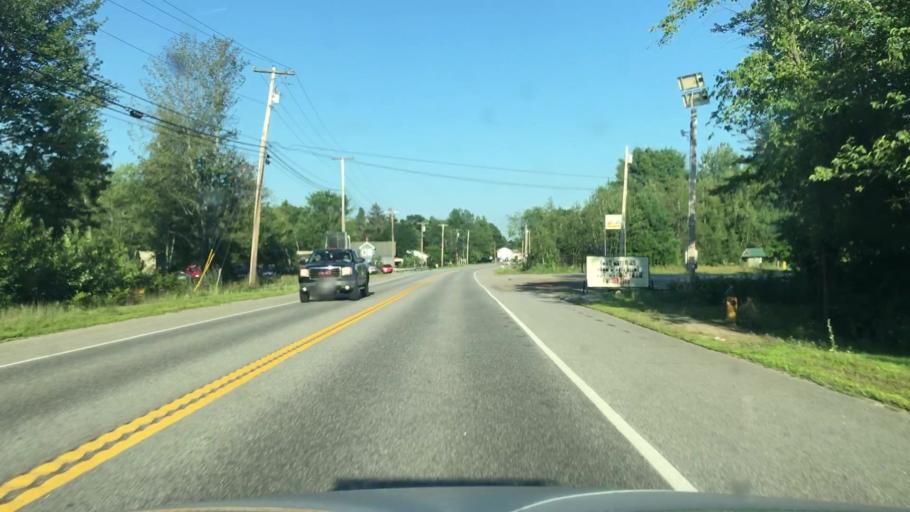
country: US
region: Maine
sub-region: Androscoggin County
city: Lisbon
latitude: 44.0505
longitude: -70.1296
